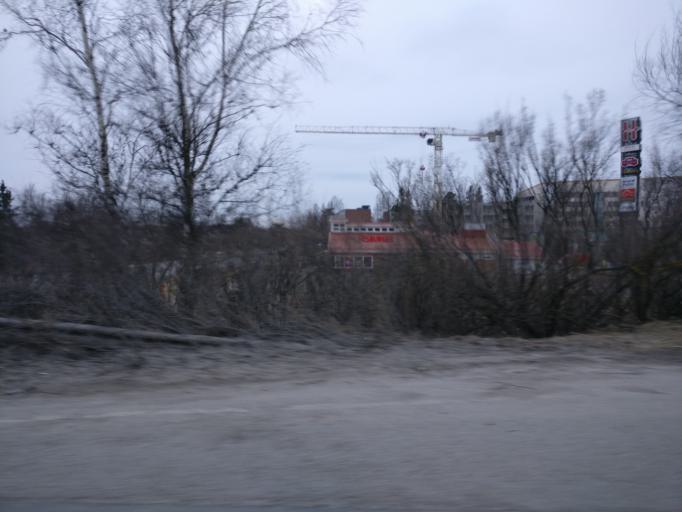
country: FI
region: Uusimaa
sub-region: Helsinki
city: Teekkarikylae
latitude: 60.2783
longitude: 24.8684
